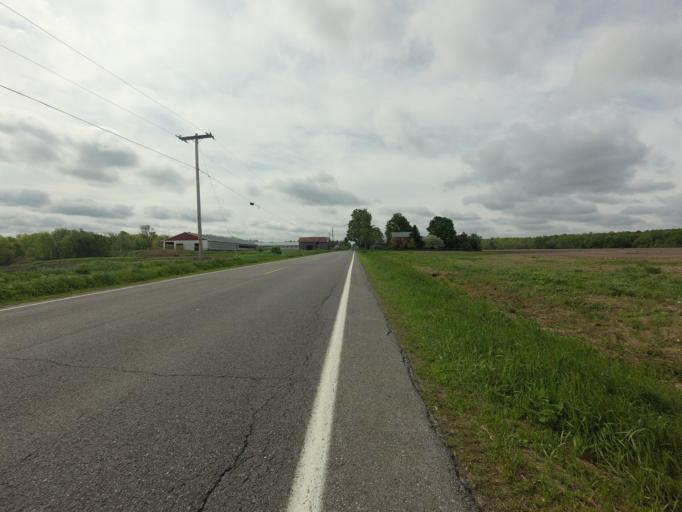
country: CA
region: Ontario
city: Cornwall
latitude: 44.7530
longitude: -74.6687
